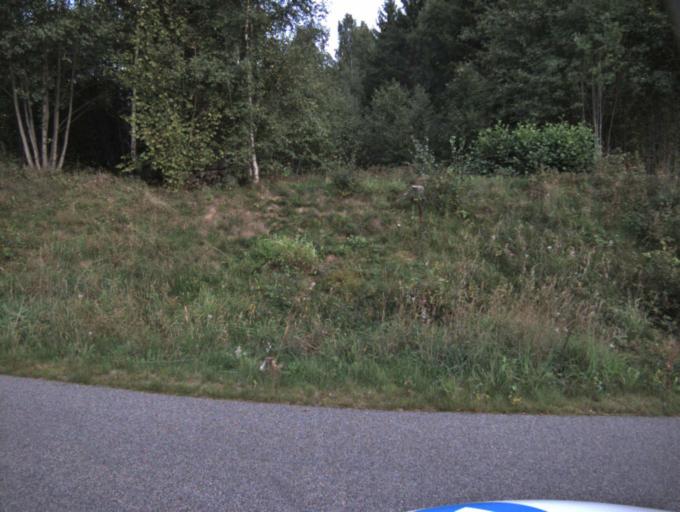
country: SE
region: Vaestra Goetaland
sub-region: Ulricehamns Kommun
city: Ulricehamn
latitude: 57.7728
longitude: 13.4077
